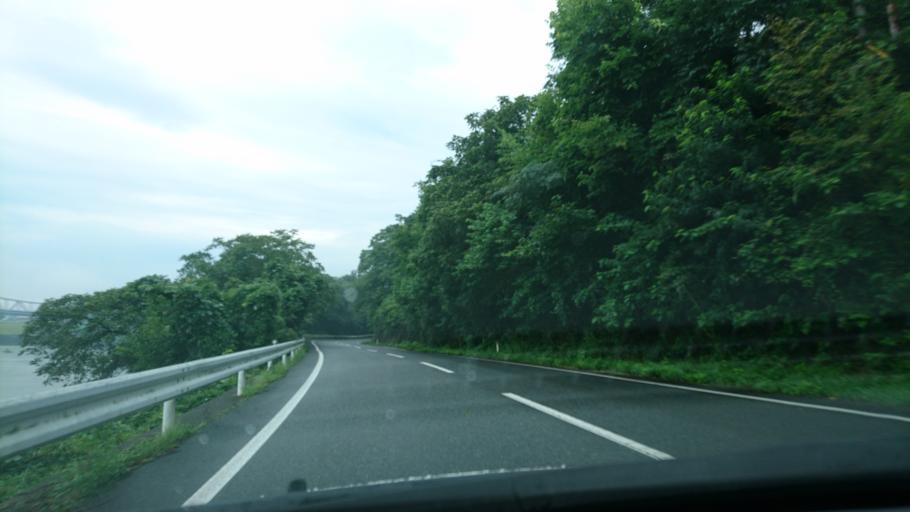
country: JP
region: Iwate
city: Ichinoseki
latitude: 38.8943
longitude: 141.2677
